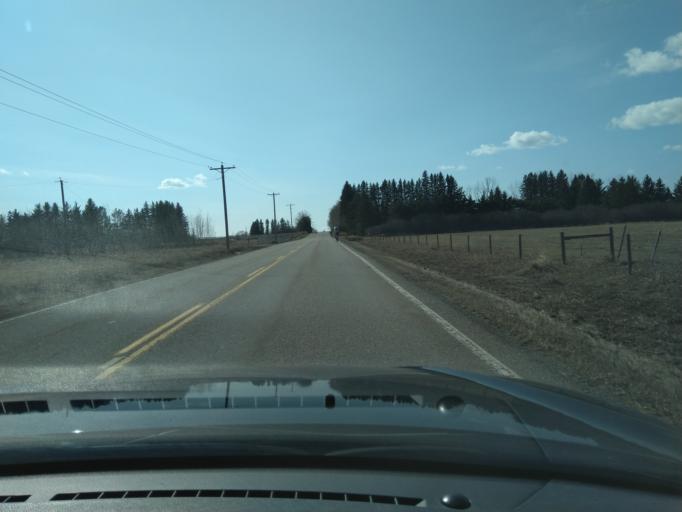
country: CA
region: Alberta
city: Cochrane
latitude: 51.0961
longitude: -114.3358
